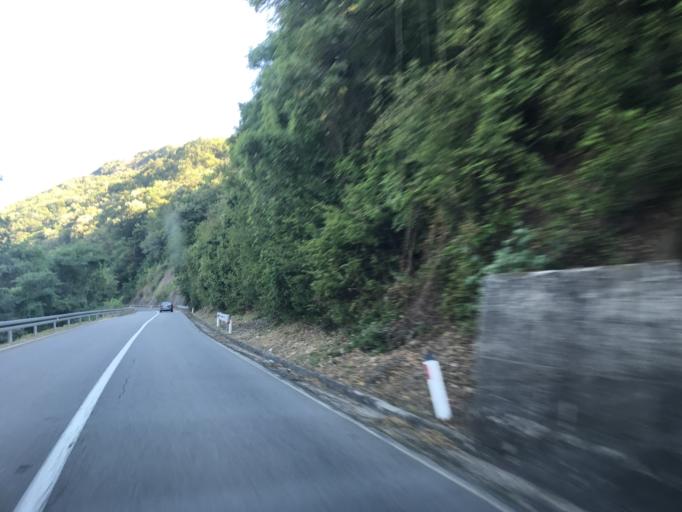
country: RO
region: Mehedinti
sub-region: Comuna Svinita
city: Svinita
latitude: 44.4904
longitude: 22.0724
